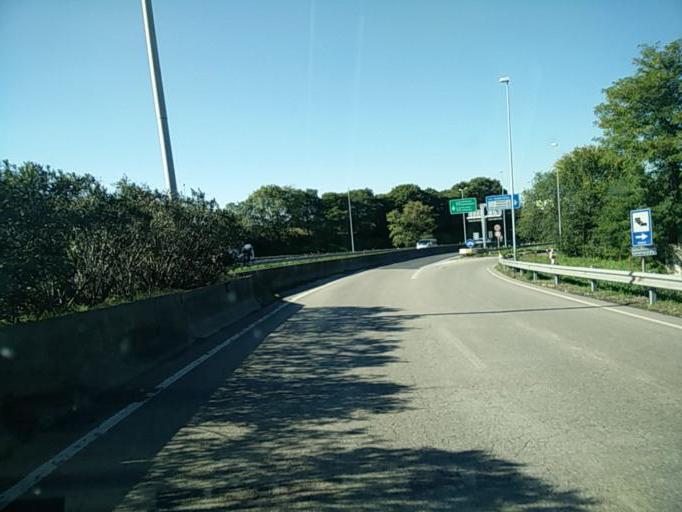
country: IT
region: Veneto
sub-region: Provincia di Verona
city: Caselle
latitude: 45.4299
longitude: 10.9117
